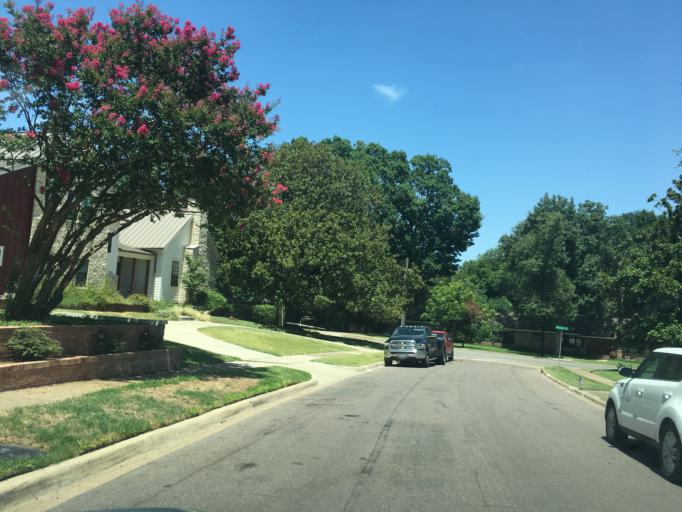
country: US
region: Texas
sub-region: Dallas County
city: Highland Park
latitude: 32.8470
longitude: -96.7344
